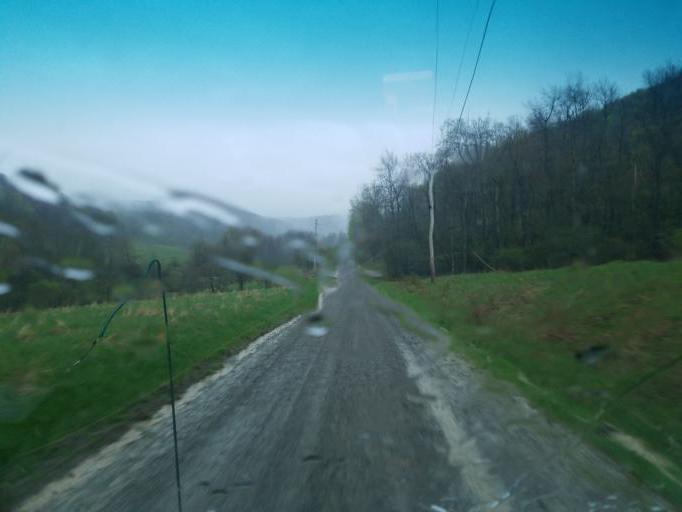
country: US
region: Pennsylvania
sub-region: Tioga County
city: Westfield
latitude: 41.9002
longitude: -77.7146
